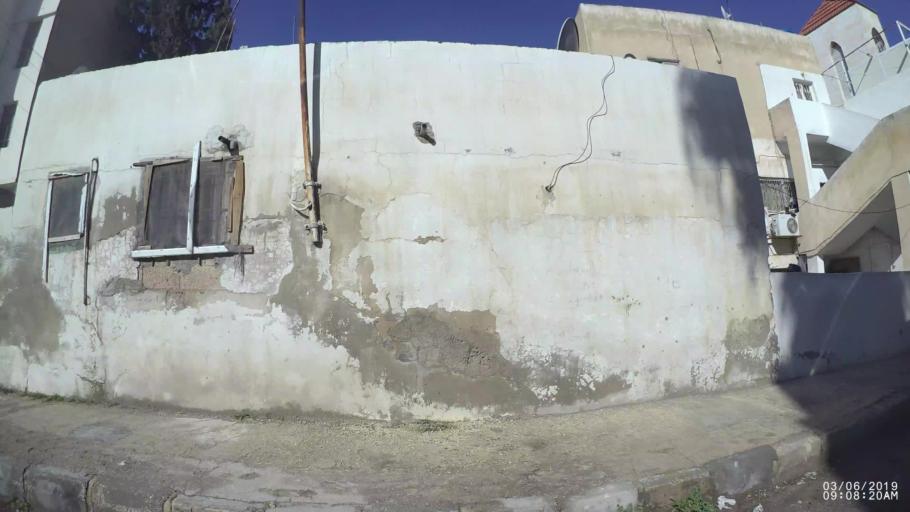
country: JO
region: Amman
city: Amman
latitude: 31.9857
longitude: 35.9894
